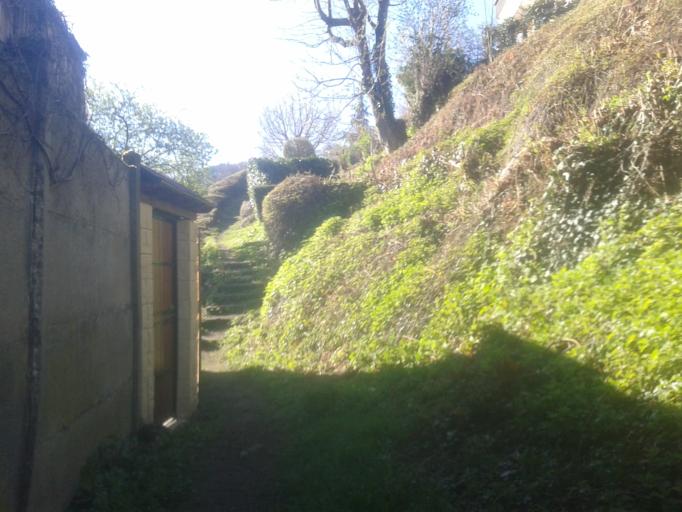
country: FR
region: Auvergne
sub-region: Departement du Puy-de-Dome
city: Chamalieres
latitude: 45.7666
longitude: 3.0649
